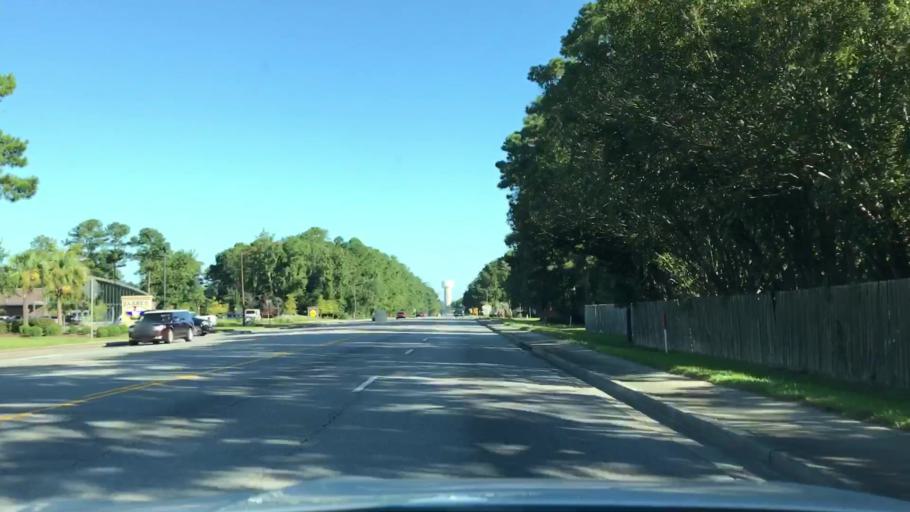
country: US
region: South Carolina
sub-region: Berkeley County
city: Goose Creek
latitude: 33.0249
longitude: -80.0553
